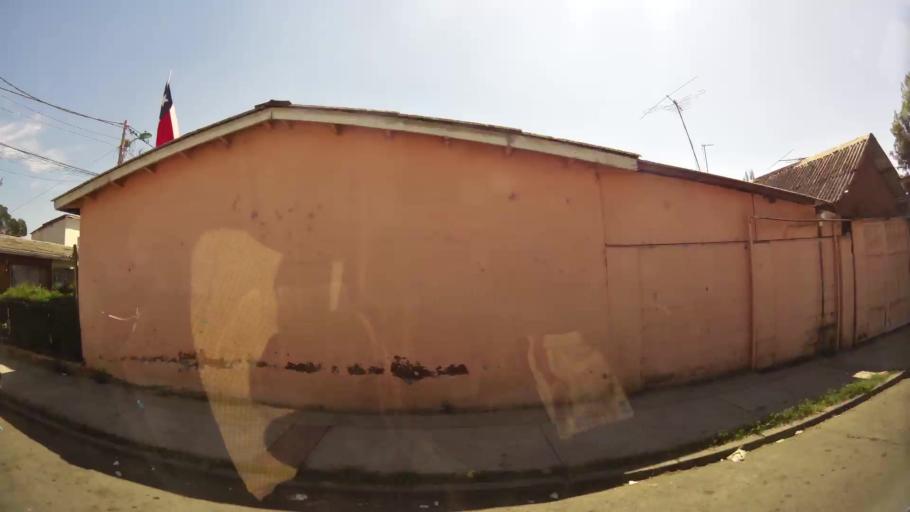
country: CL
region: Santiago Metropolitan
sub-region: Provincia de Talagante
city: Talagante
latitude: -33.6541
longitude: -70.9231
